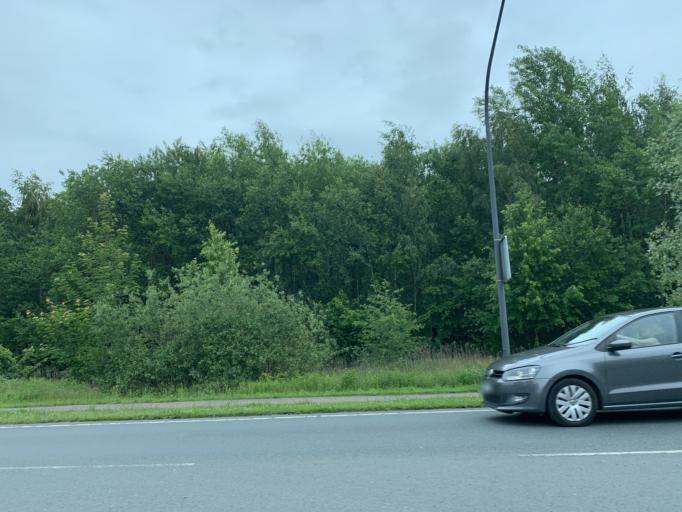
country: DE
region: North Rhine-Westphalia
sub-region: Regierungsbezirk Arnsberg
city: Hamm
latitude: 51.6558
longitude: 7.8384
